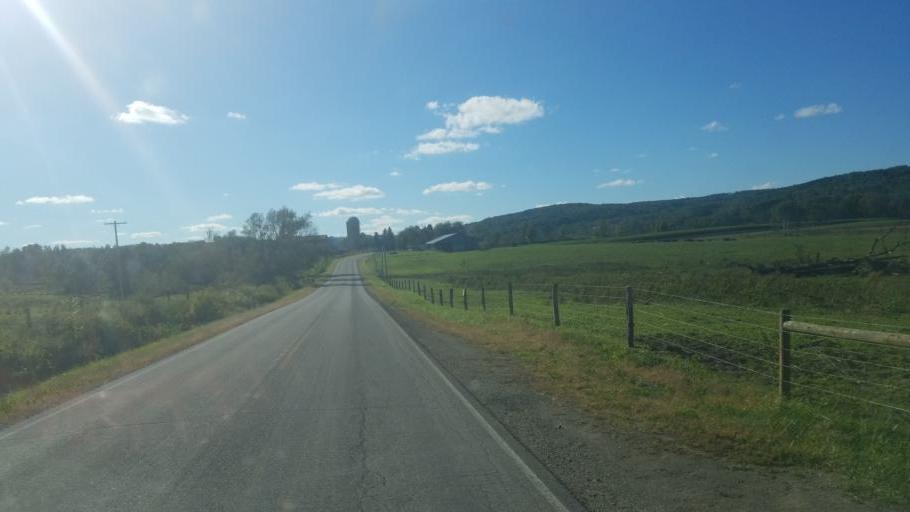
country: US
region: New York
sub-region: Allegany County
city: Cuba
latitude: 42.2745
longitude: -78.2029
